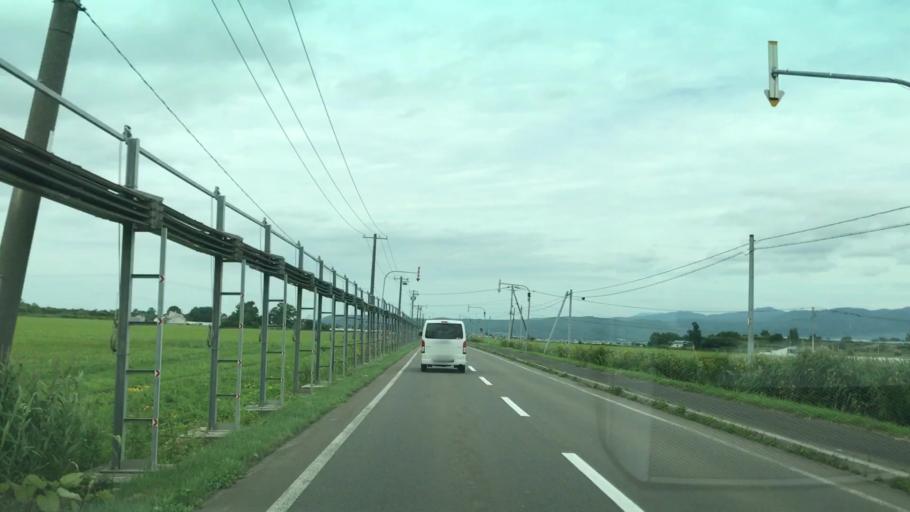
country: JP
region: Hokkaido
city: Iwanai
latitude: 42.9956
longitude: 140.5972
